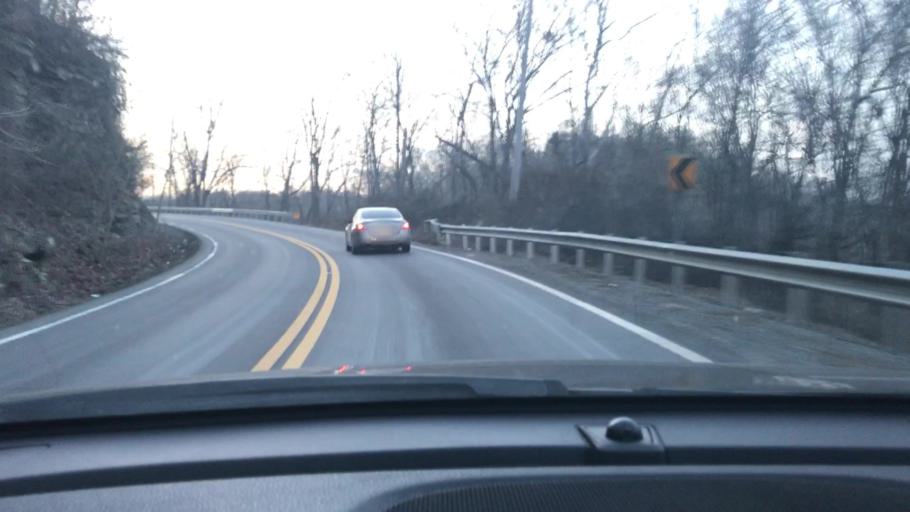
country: US
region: Tennessee
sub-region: Cheatham County
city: Ashland City
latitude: 36.2826
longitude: -87.1070
